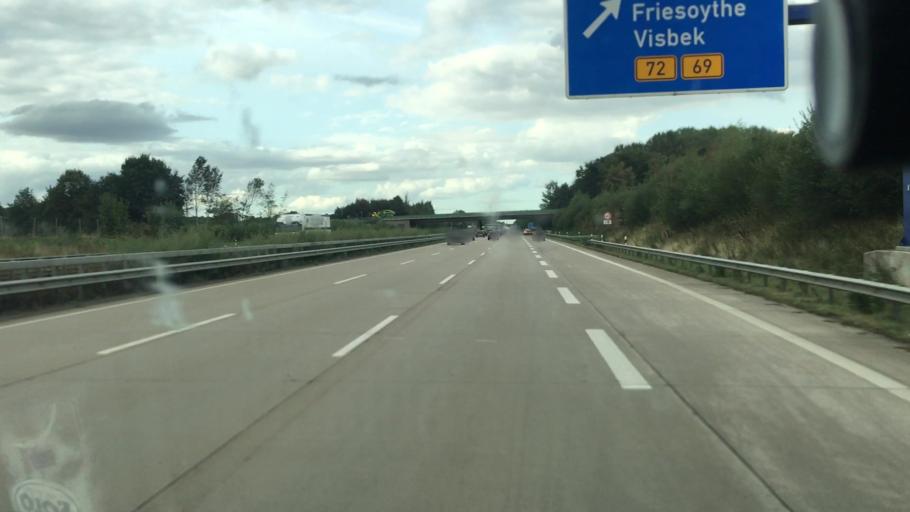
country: DE
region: Lower Saxony
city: Buehren
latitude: 52.8102
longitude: 8.2101
